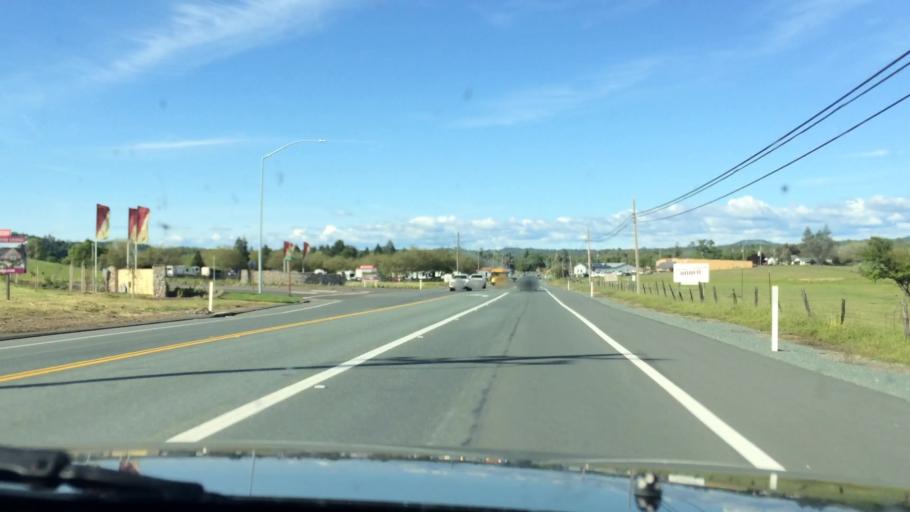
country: US
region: California
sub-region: Amador County
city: Plymouth
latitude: 38.4692
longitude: -120.8534
